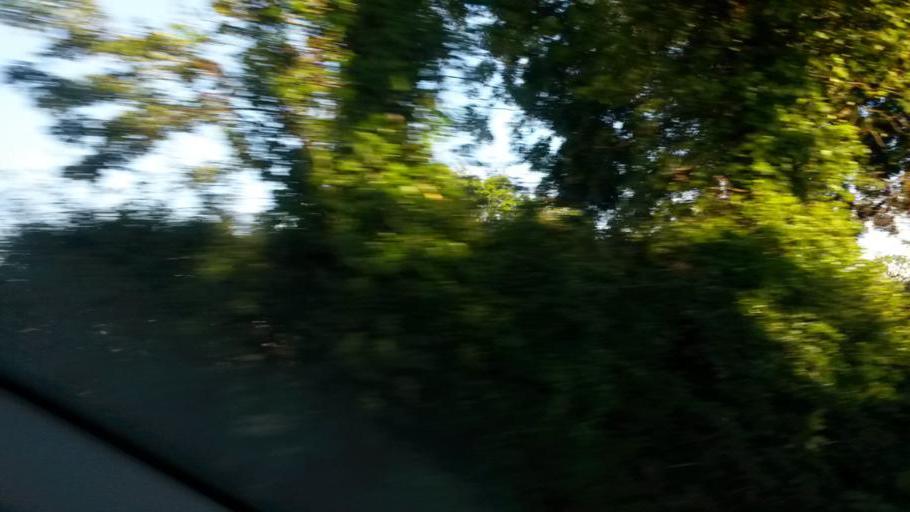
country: IE
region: Leinster
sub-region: An Mhi
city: Ashbourne
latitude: 53.4798
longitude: -6.3162
